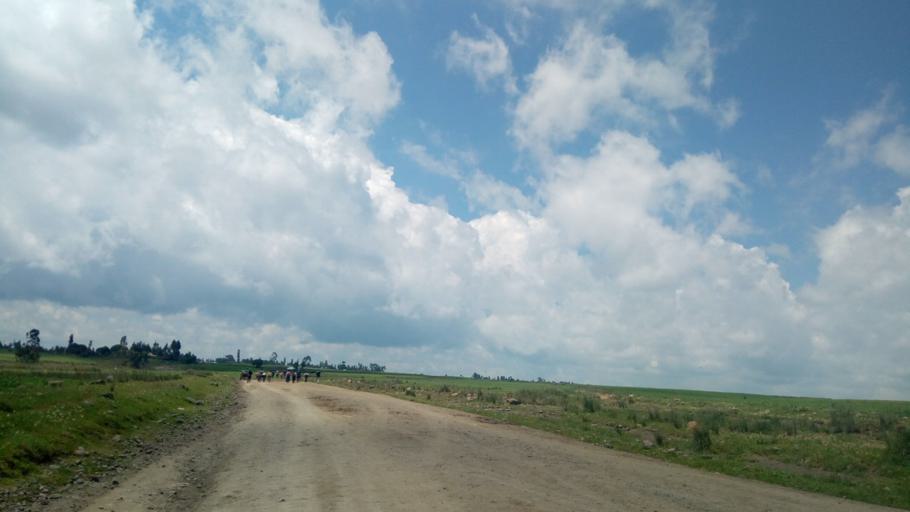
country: ET
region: Oromiya
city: Sendafa
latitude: 8.9857
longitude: 39.1254
